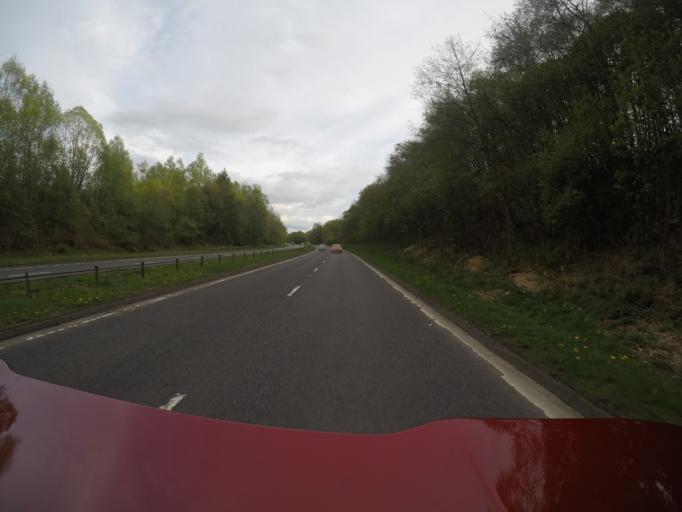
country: GB
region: Scotland
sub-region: West Dunbartonshire
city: Alexandria
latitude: 55.9935
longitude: -4.5946
